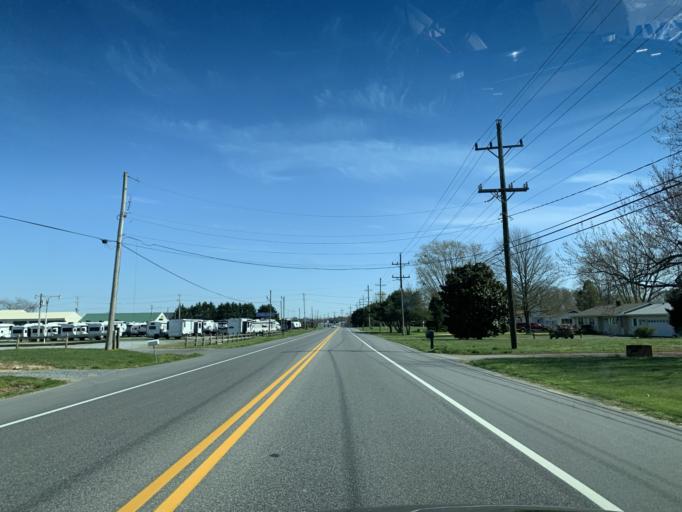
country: US
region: Delaware
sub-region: Sussex County
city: Milford
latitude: 38.9247
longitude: -75.4553
